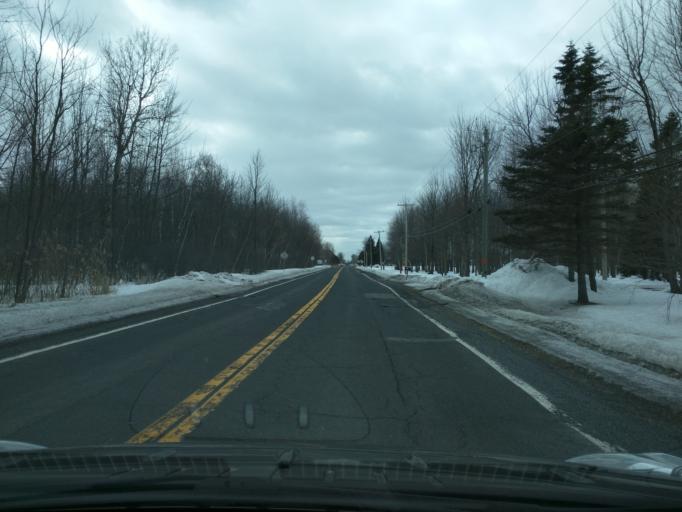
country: CA
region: Quebec
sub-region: Monteregie
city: Sainte-Julie
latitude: 45.6807
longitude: -73.2621
